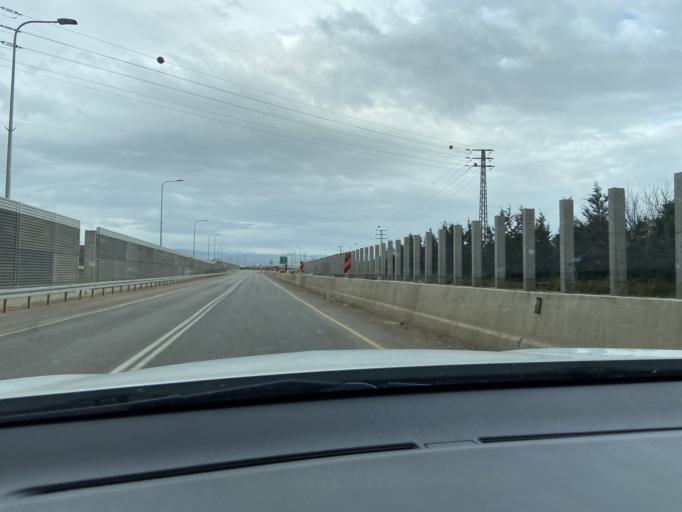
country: IL
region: Northern District
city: El Mazra`a
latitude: 32.9804
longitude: 35.1018
